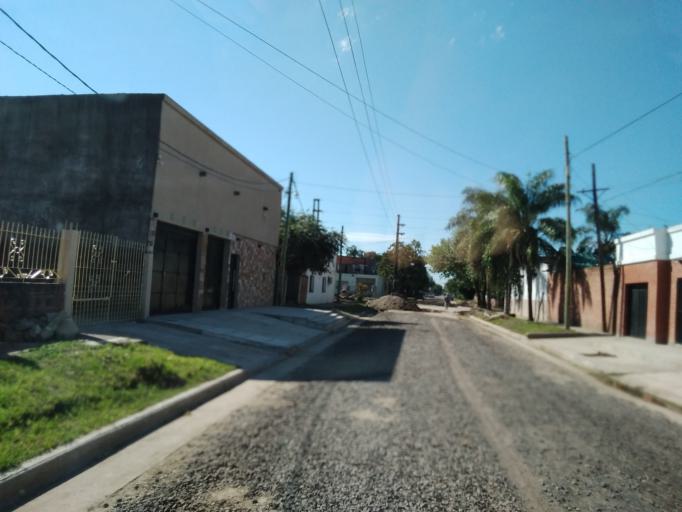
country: AR
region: Corrientes
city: Corrientes
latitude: -27.4811
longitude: -58.8102
